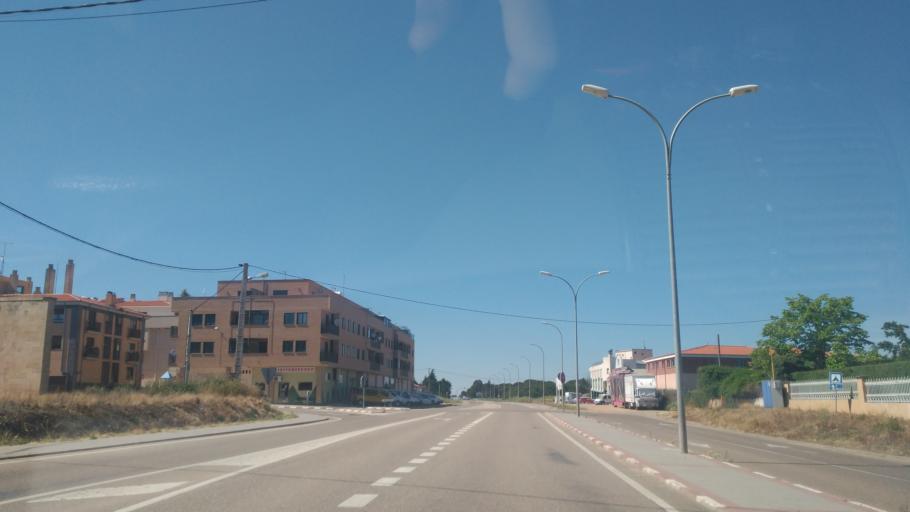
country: ES
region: Castille and Leon
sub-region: Provincia de Salamanca
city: Villares de la Reina
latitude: 41.0196
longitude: -5.6704
